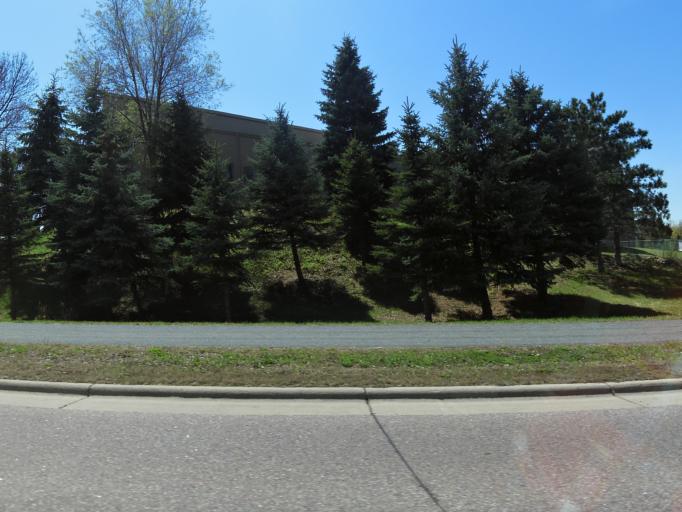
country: US
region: Minnesota
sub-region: Hennepin County
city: Eden Prairie
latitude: 44.8260
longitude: -93.4156
